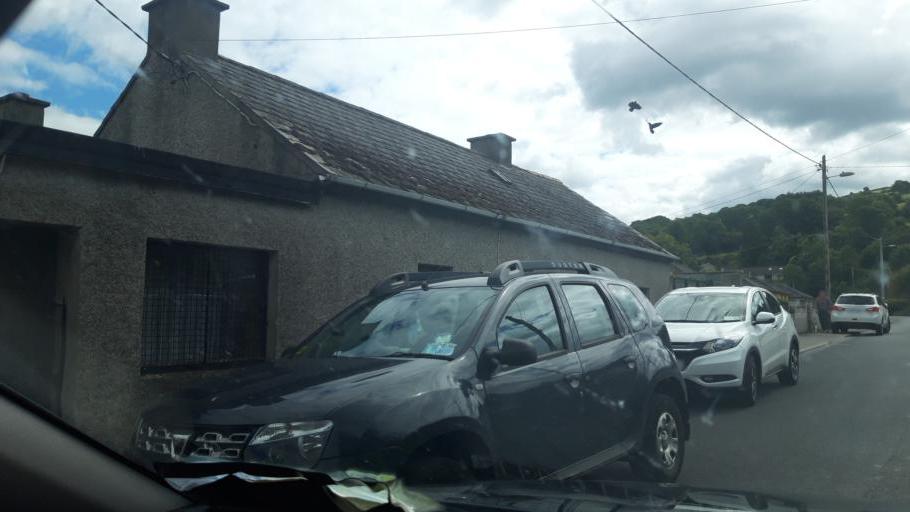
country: IE
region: Munster
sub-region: South Tipperary
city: Cluain Meala
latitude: 52.3486
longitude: -7.7042
